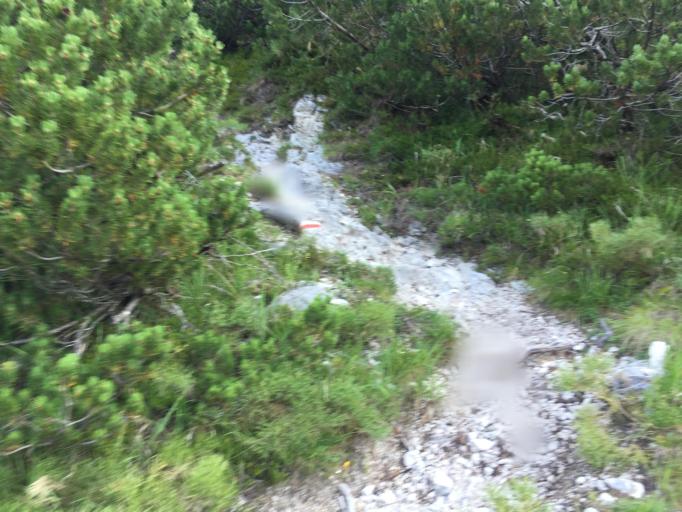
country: IT
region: Friuli Venezia Giulia
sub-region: Provincia di Udine
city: Malborghetto
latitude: 46.4668
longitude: 13.4319
